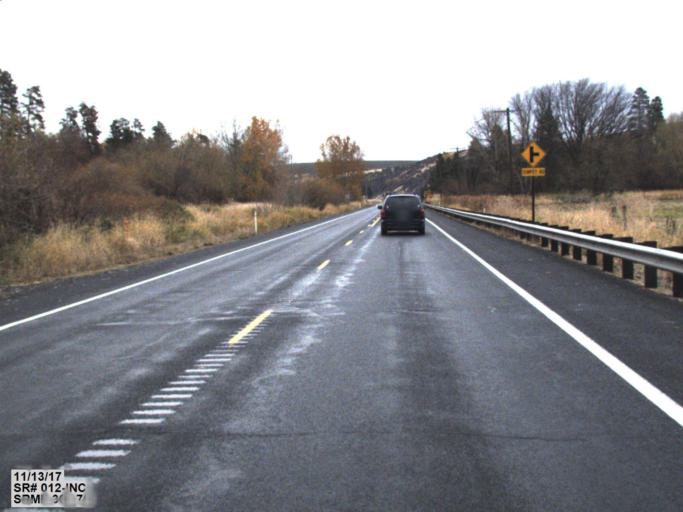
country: US
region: Washington
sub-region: Walla Walla County
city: Waitsburg
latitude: 46.2883
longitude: -118.0770
